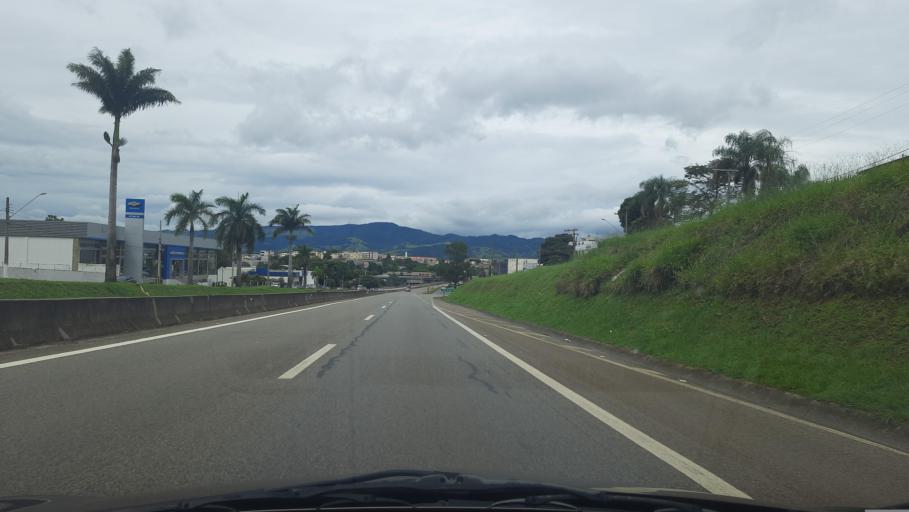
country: BR
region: Sao Paulo
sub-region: Sao Joao Da Boa Vista
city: Sao Joao da Boa Vista
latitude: -21.9842
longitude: -46.7879
